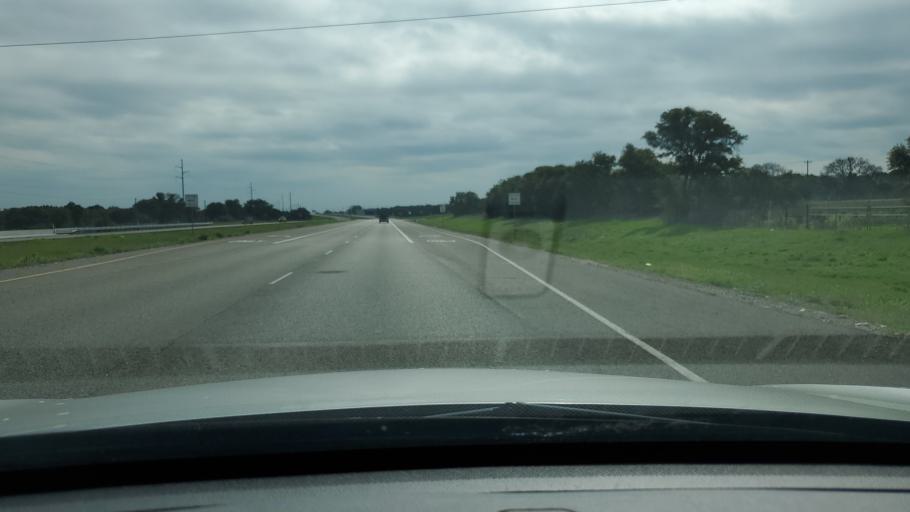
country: US
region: Texas
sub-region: Williamson County
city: Serenada
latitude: 30.7535
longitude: -97.7168
